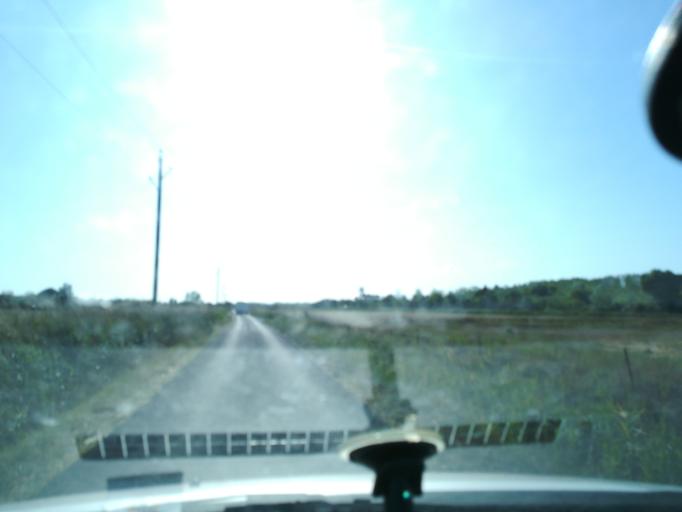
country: FR
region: Languedoc-Roussillon
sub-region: Departement de l'Herault
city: Vias
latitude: 43.2911
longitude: 3.3786
